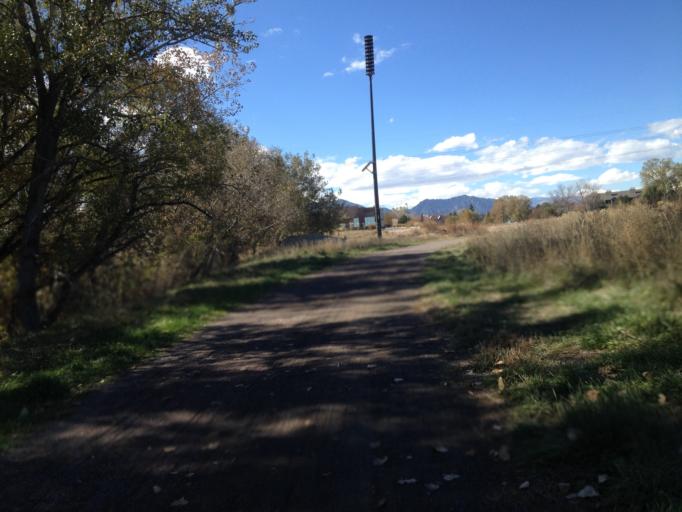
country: US
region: Colorado
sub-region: Boulder County
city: Superior
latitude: 39.9578
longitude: -105.1547
